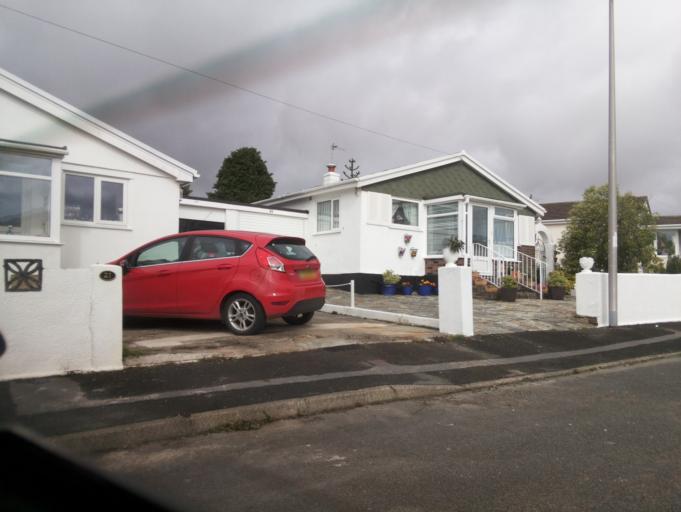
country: GB
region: England
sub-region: Devon
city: Dartmouth
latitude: 50.3300
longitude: -3.5984
